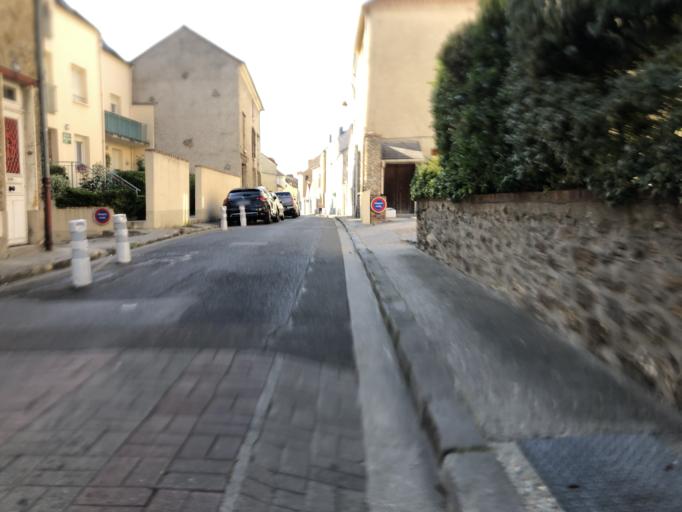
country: FR
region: Ile-de-France
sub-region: Departement des Yvelines
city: Triel-sur-Seine
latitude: 48.9770
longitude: 2.0075
